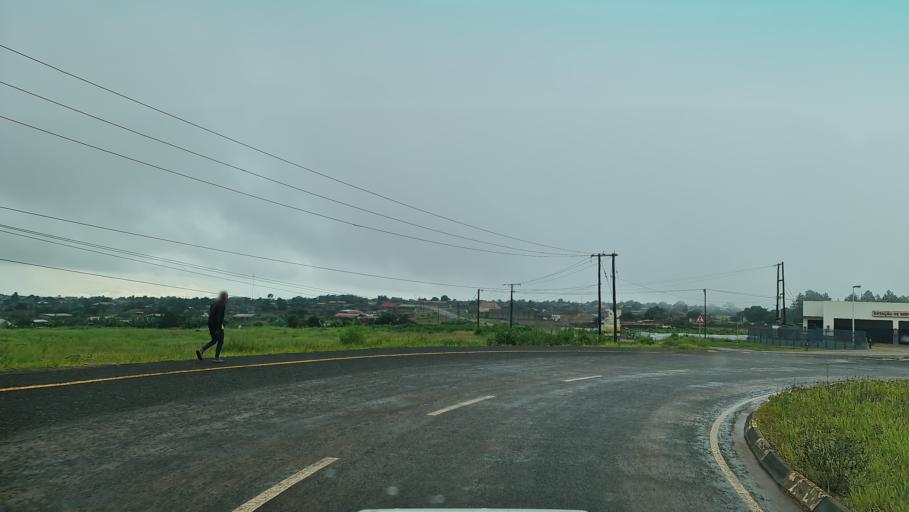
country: MZ
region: Niassa
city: Lichinga
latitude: -13.3371
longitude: 35.2504
